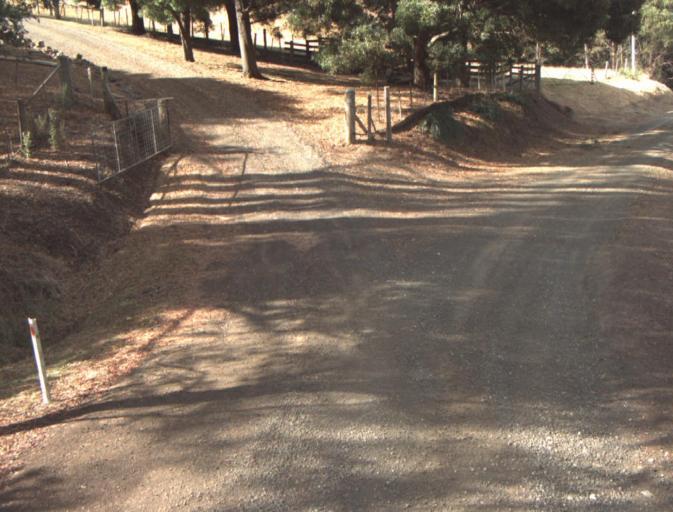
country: AU
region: Tasmania
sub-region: Launceston
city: Mayfield
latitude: -41.2946
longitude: 147.2153
